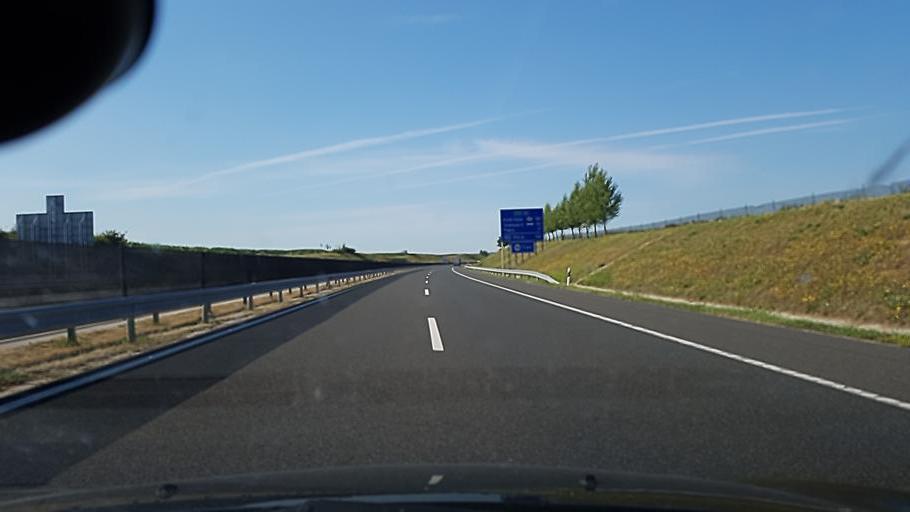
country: HU
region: Tolna
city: Madocsa
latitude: 46.7218
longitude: 18.8768
